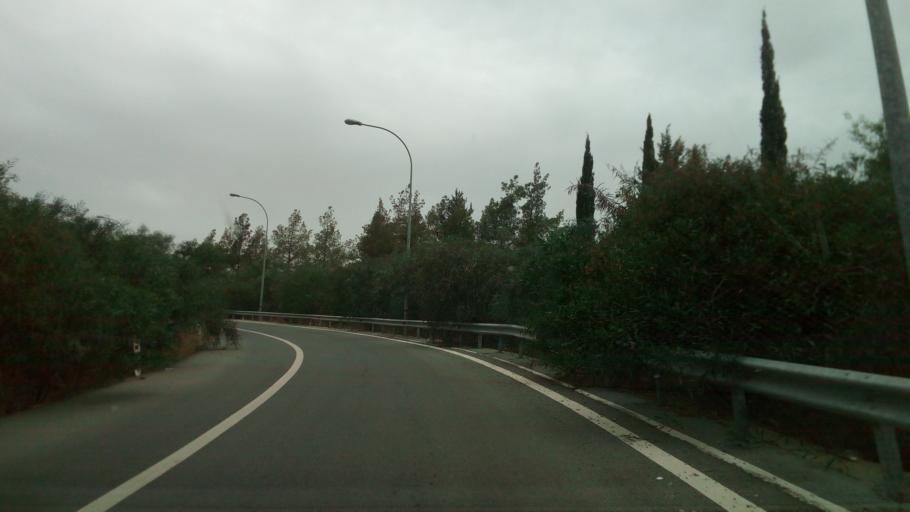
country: CY
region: Larnaka
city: Kofinou
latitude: 34.8403
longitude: 33.3987
